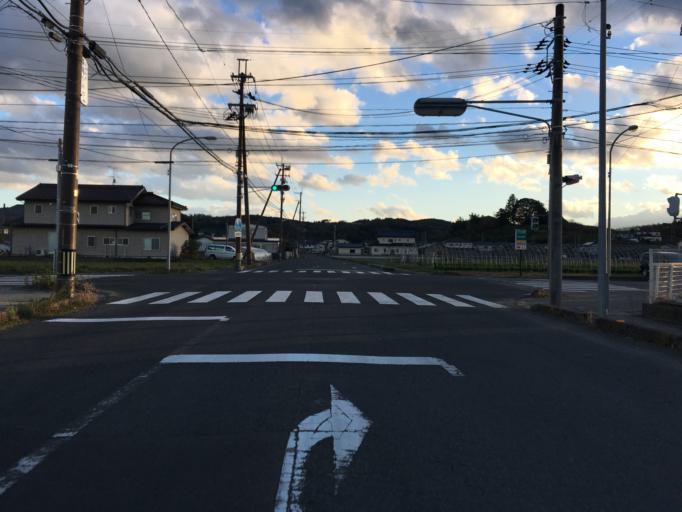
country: JP
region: Fukushima
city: Hobaramachi
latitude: 37.8090
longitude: 140.5516
